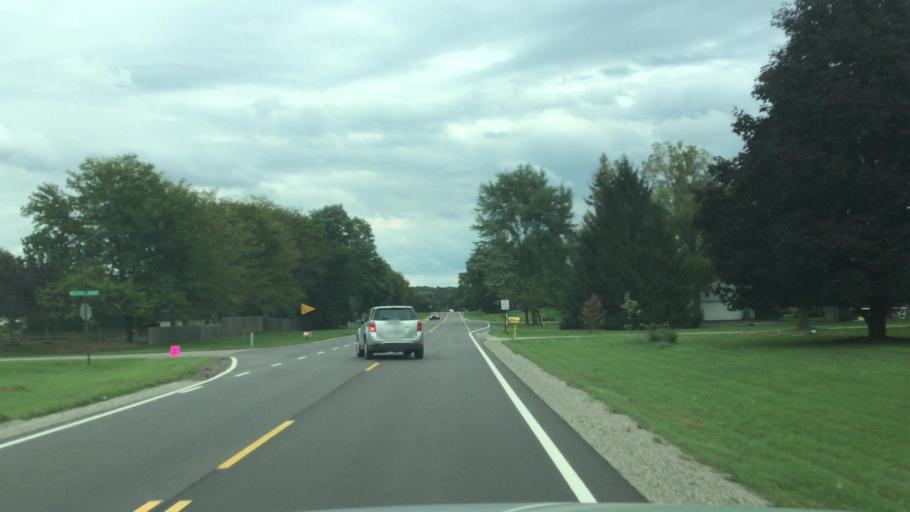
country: US
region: Michigan
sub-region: Livingston County
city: Brighton
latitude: 42.4707
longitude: -83.8144
